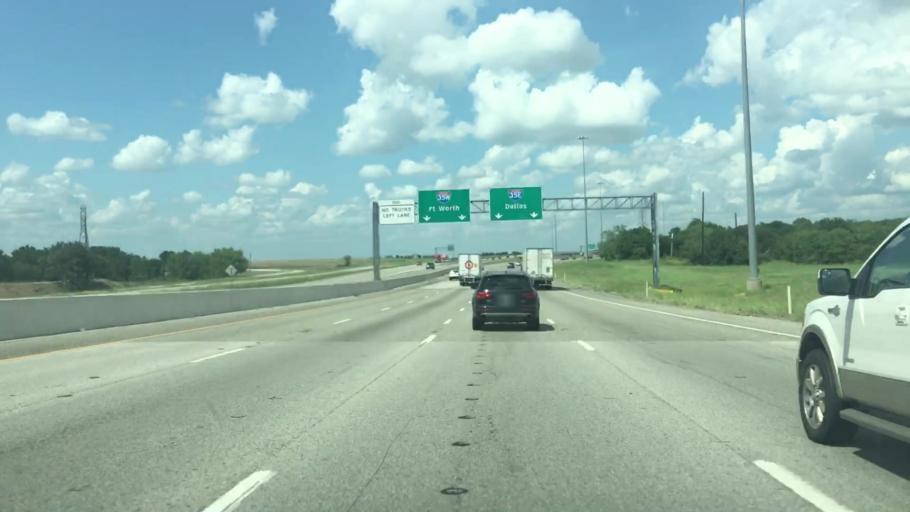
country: US
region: Texas
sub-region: Hill County
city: Hillsboro
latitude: 32.0464
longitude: -97.0947
